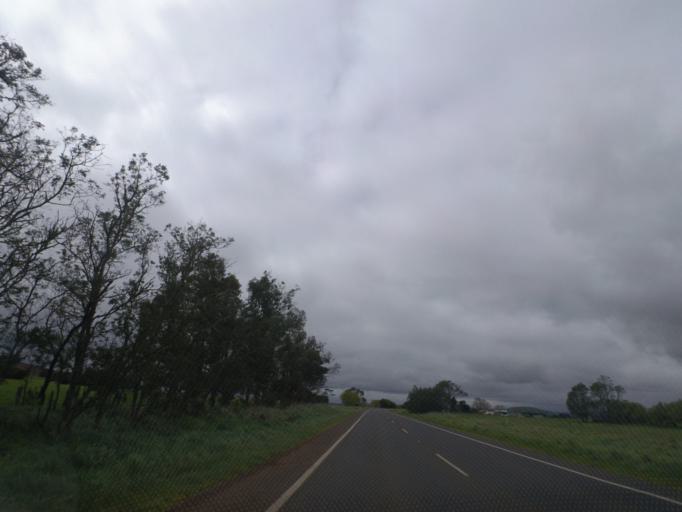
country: AU
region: Victoria
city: Brown Hill
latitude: -37.4080
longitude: 143.9585
